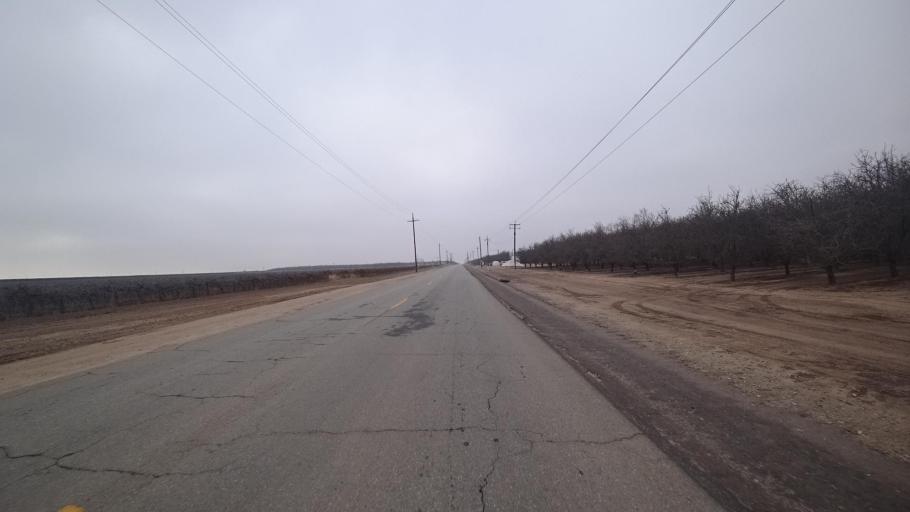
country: US
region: California
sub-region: Kern County
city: Maricopa
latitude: 35.0938
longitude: -119.2723
